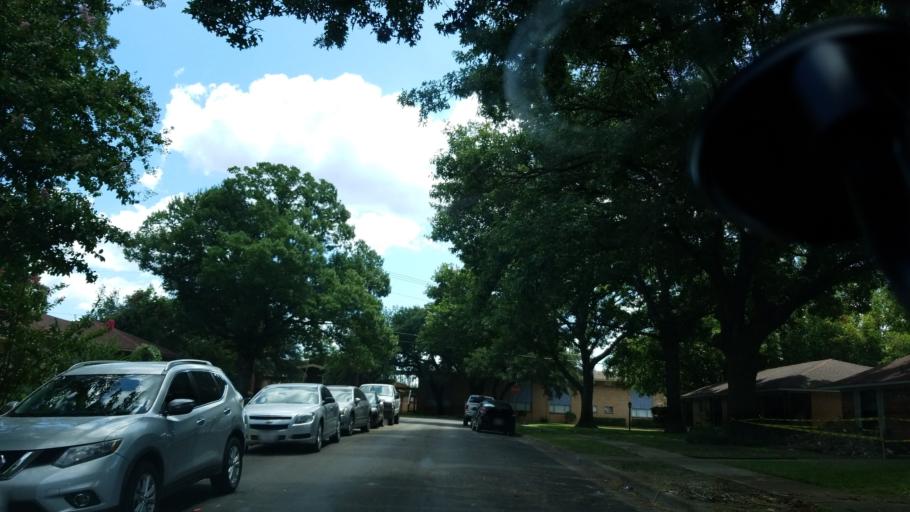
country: US
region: Texas
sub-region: Dallas County
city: Cockrell Hill
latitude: 32.7013
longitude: -96.8429
